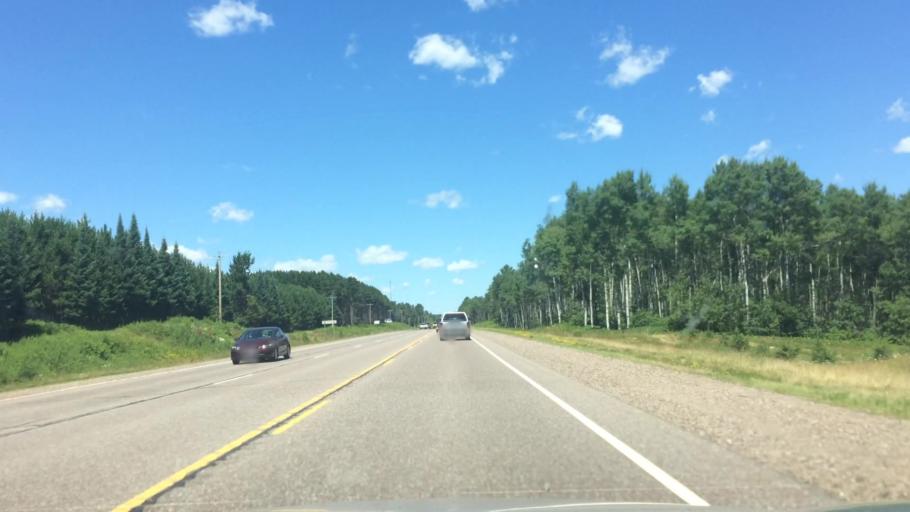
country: US
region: Wisconsin
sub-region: Lincoln County
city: Tomahawk
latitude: 45.6674
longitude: -89.7141
